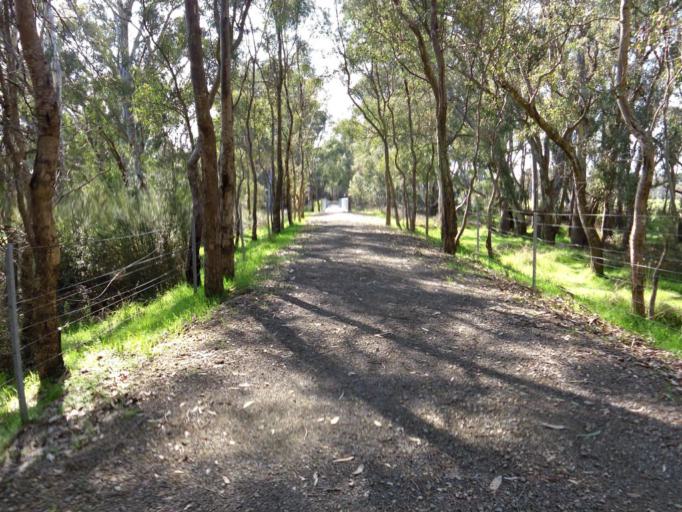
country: AU
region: Victoria
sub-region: Murrindindi
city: Alexandra
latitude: -37.1577
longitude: 145.5703
